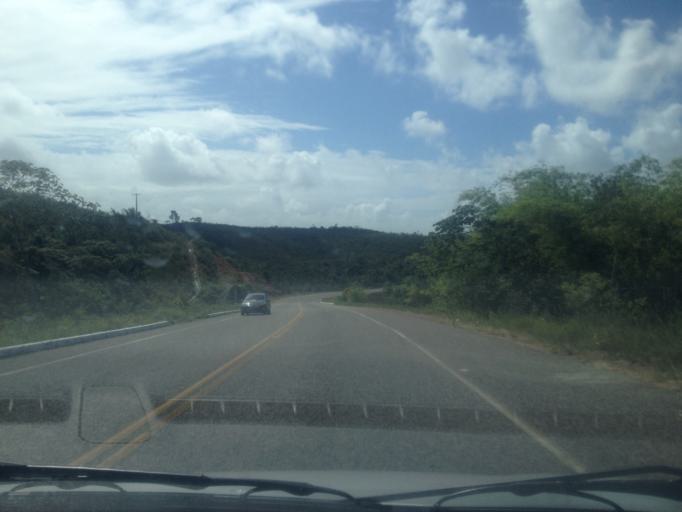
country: BR
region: Bahia
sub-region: Conde
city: Conde
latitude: -11.9110
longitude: -37.6576
